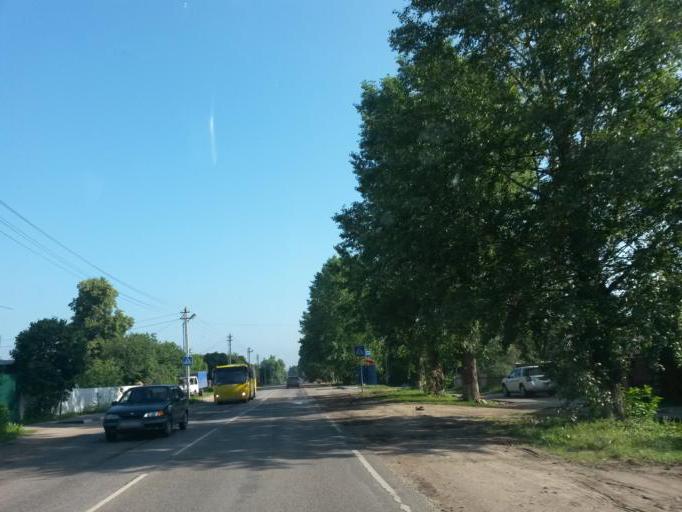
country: RU
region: Moskovskaya
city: Yam
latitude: 55.4815
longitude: 37.7512
